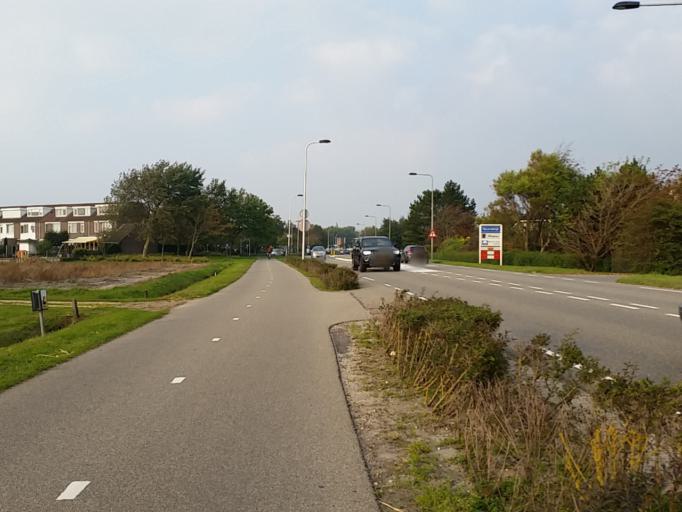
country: NL
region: South Holland
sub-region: Gemeente Noordwijk
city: Noordwijk-Binnen
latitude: 52.2243
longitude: 4.4426
